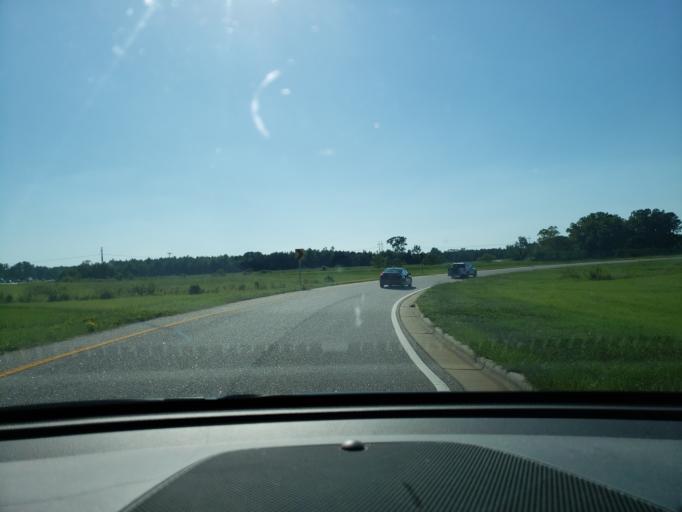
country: US
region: North Carolina
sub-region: Robeson County
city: Fairmont
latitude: 34.5919
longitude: -79.1144
